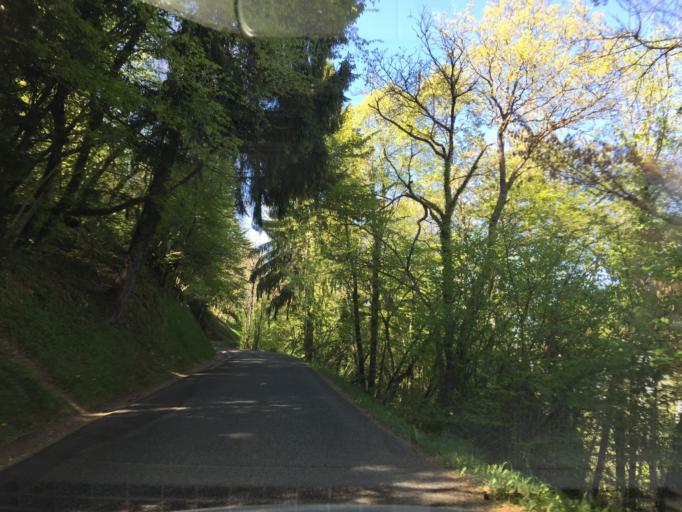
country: FR
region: Rhone-Alpes
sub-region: Departement de la Savoie
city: La Motte-Servolex
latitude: 45.5840
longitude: 5.8306
